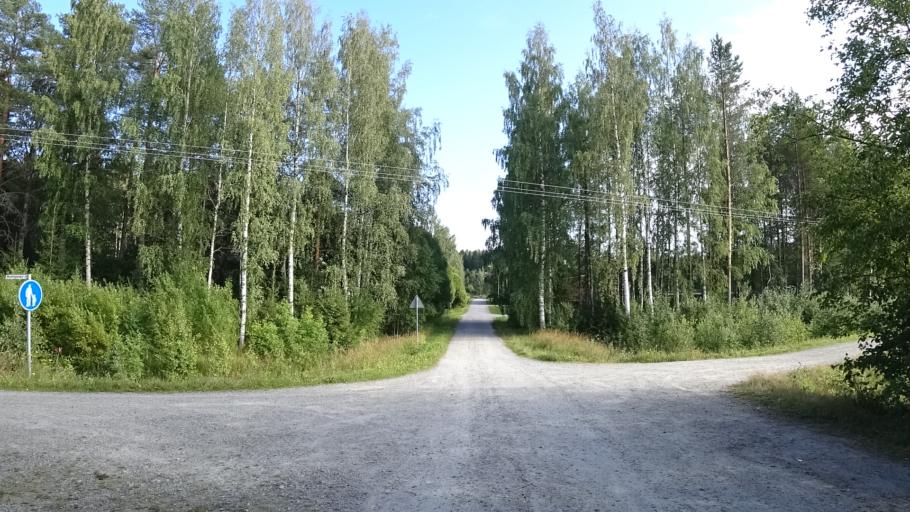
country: FI
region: North Karelia
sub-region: Joensuu
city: Eno
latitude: 62.8012
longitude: 30.1484
